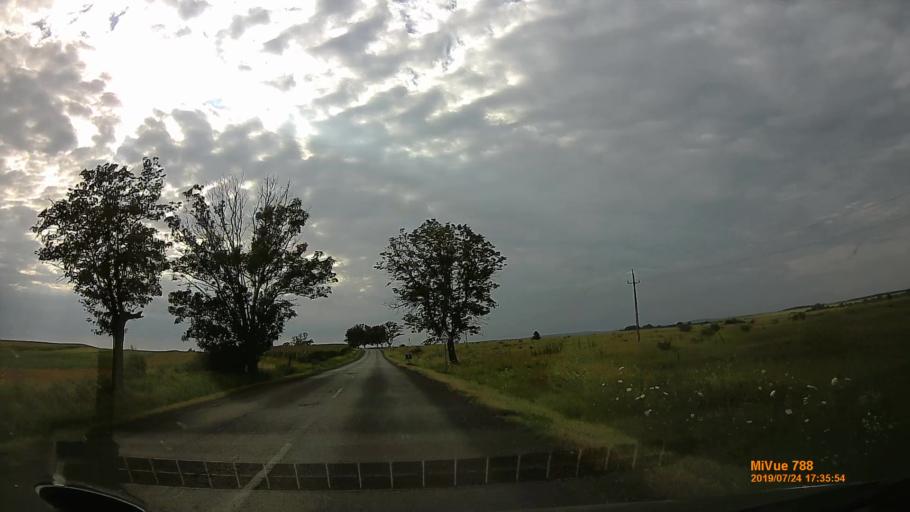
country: HU
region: Borsod-Abauj-Zemplen
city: Abaujszanto
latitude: 48.3112
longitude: 21.1837
